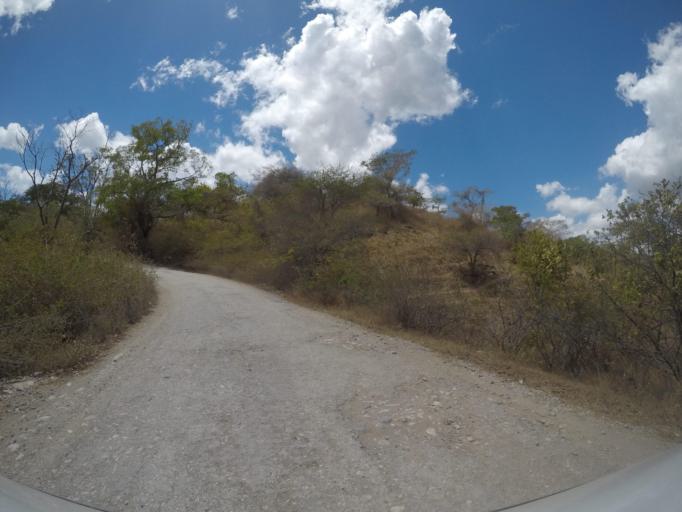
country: TL
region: Baucau
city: Baucau
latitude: -8.4848
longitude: 126.6206
